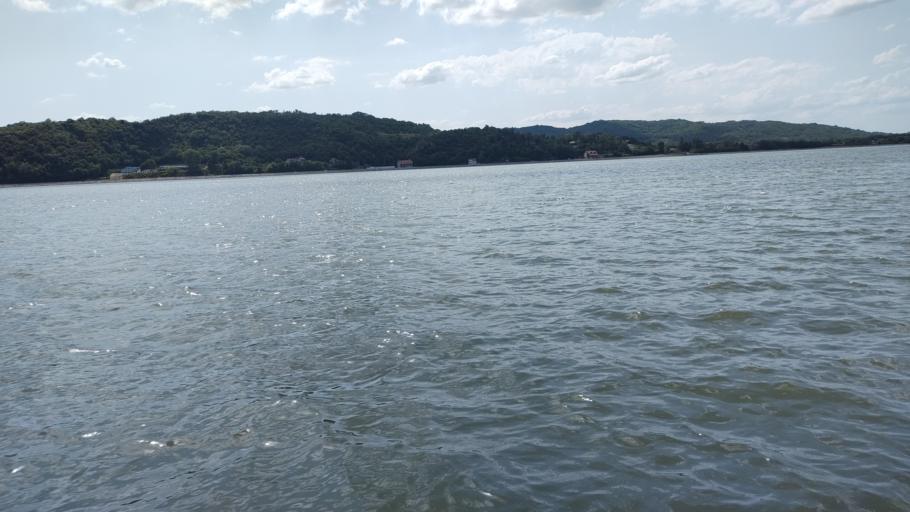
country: RS
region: Central Serbia
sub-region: Branicevski Okrug
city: Golubac
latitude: 44.6631
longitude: 21.6266
